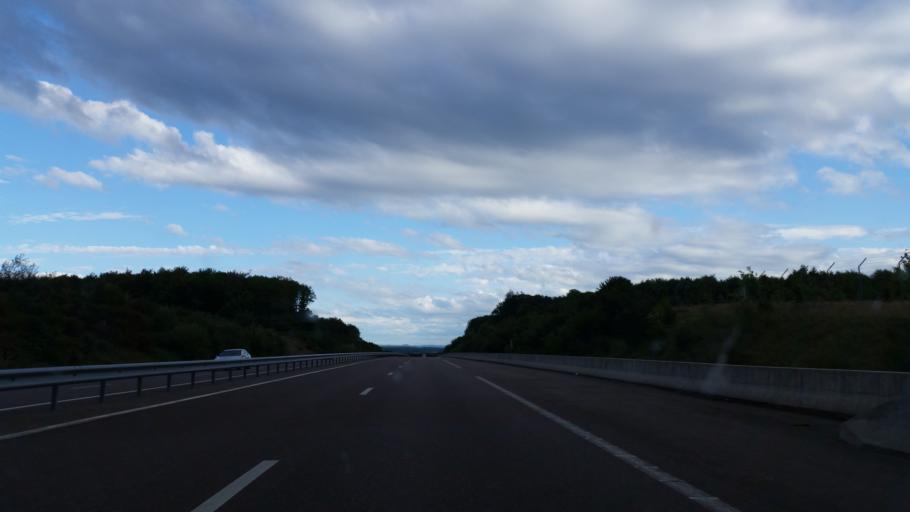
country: FR
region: Franche-Comte
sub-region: Departement de la Haute-Saone
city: Froideconche
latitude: 47.8476
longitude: 6.3892
